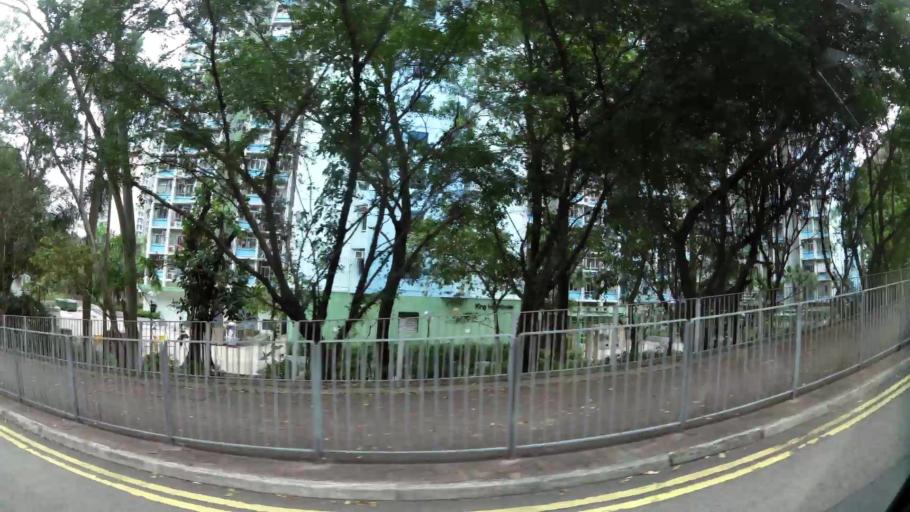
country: HK
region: Wanchai
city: Wan Chai
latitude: 22.2800
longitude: 114.2178
